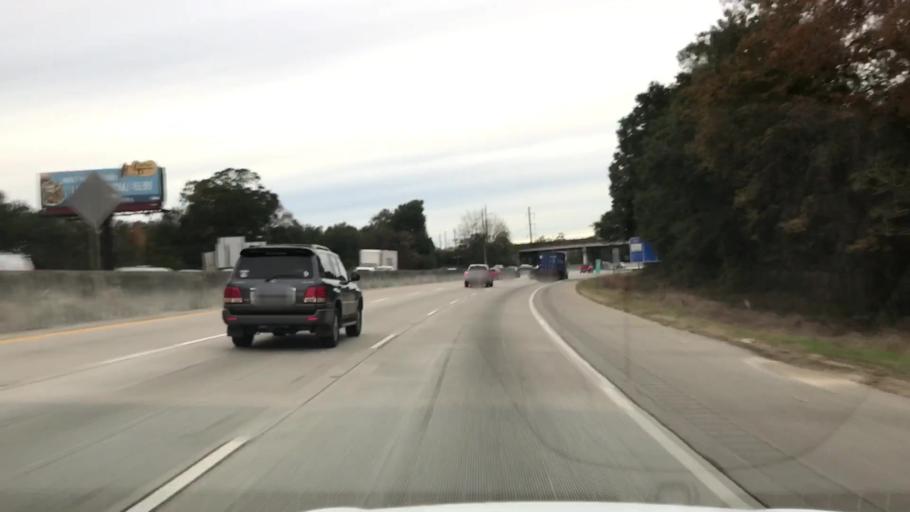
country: US
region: South Carolina
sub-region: Charleston County
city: North Charleston
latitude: 32.8456
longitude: -79.9852
